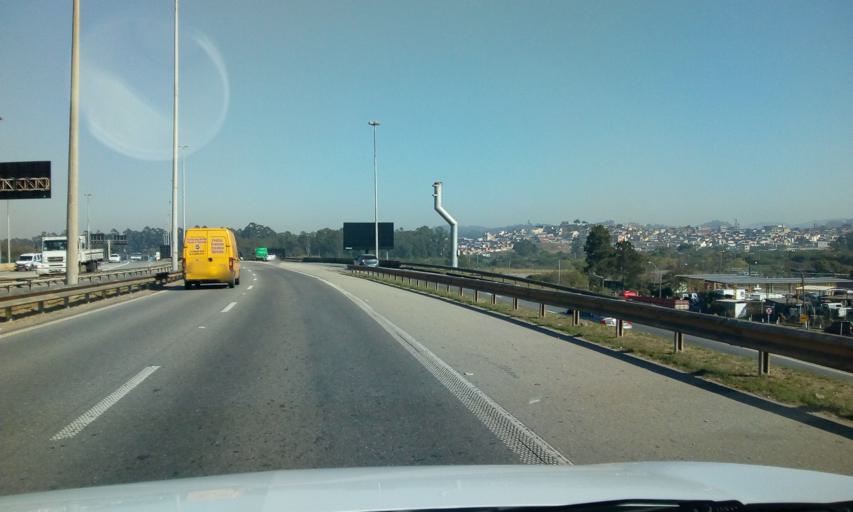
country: BR
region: Sao Paulo
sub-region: Guarulhos
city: Guarulhos
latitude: -23.4225
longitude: -46.4831
